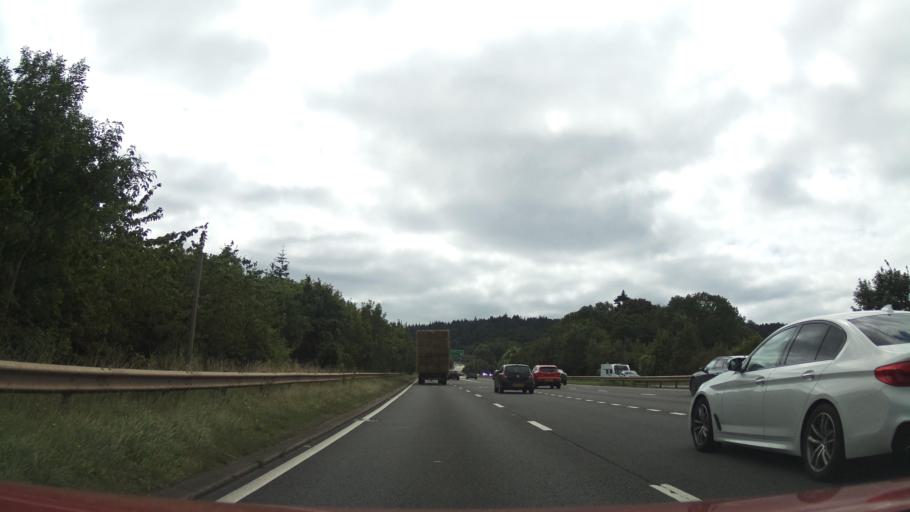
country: GB
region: England
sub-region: Devon
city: Exminster
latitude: 50.6539
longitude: -3.5412
